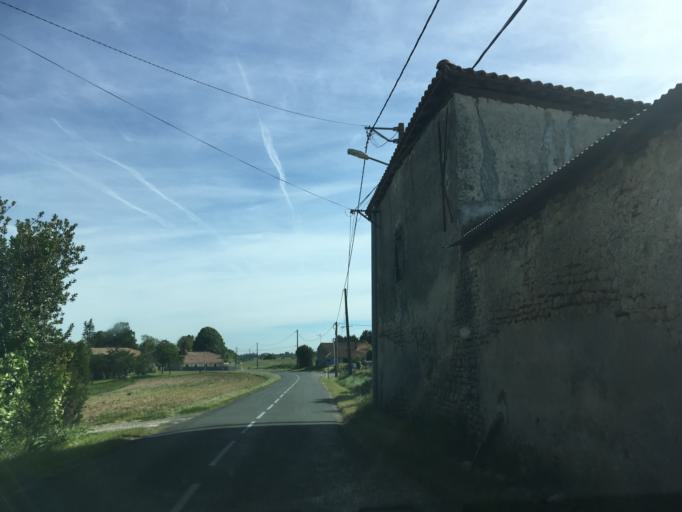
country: FR
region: Poitou-Charentes
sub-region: Departement de la Charente-Maritime
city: Mirambeau
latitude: 45.3459
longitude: -0.5866
